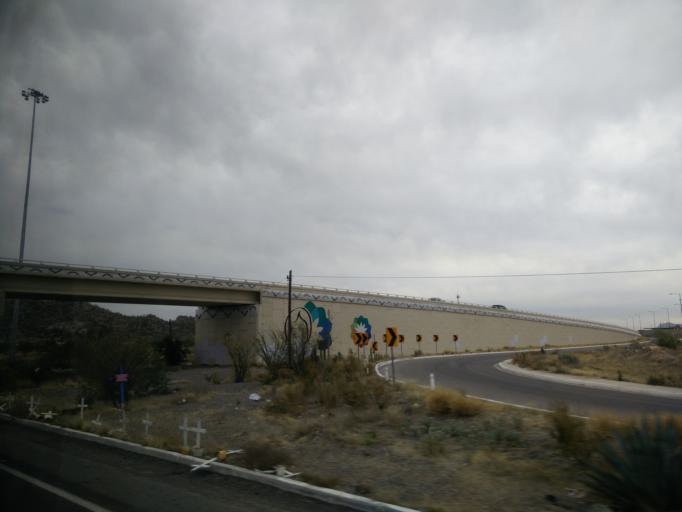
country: MX
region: Sonora
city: Hermosillo
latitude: 29.0092
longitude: -110.9642
